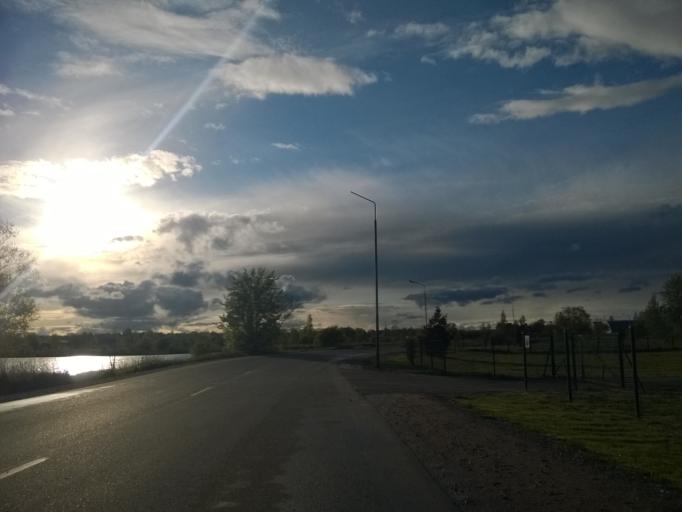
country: LV
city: Tireli
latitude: 56.9353
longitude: 23.6038
